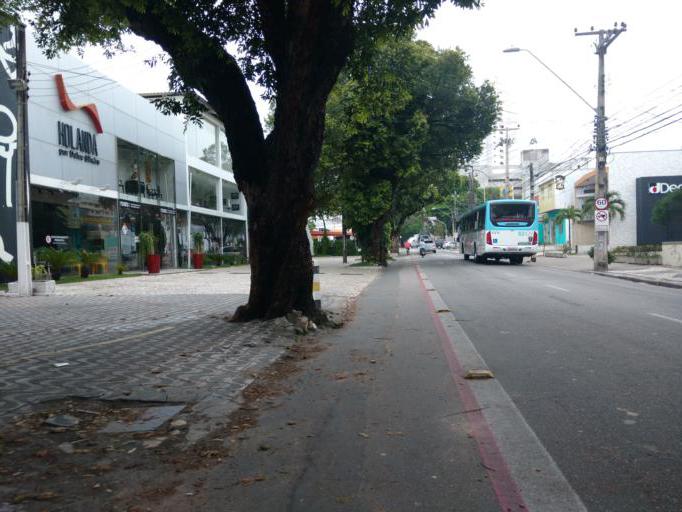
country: BR
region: Ceara
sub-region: Fortaleza
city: Fortaleza
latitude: -3.7333
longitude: -38.5071
